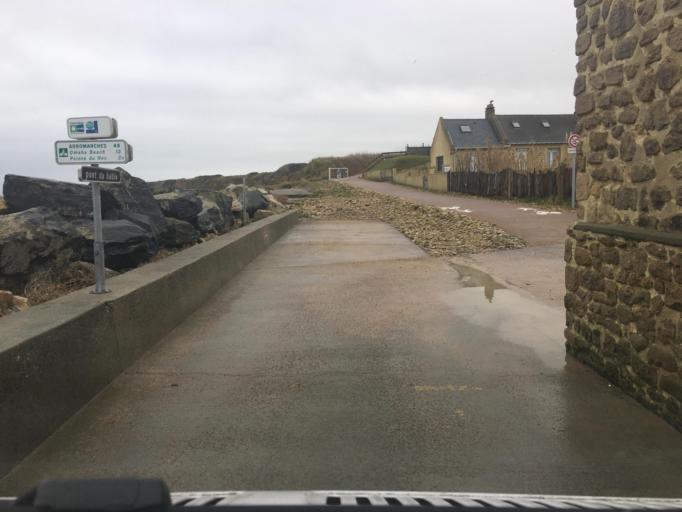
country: FR
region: Lower Normandy
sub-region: Departement du Calvados
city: Grandcamp-Maisy
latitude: 49.3934
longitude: -1.0193
